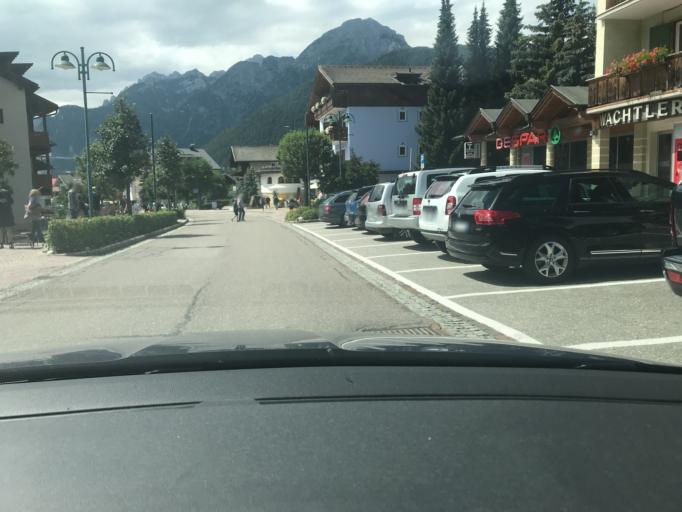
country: IT
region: Trentino-Alto Adige
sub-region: Bolzano
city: Dobbiaco
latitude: 46.7344
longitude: 12.2237
